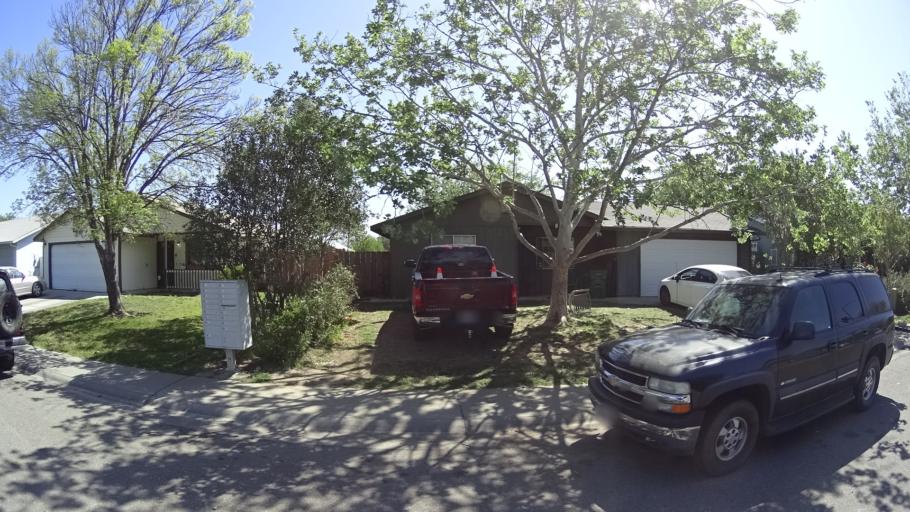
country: US
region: California
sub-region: Glenn County
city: Orland
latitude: 39.7374
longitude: -122.1810
